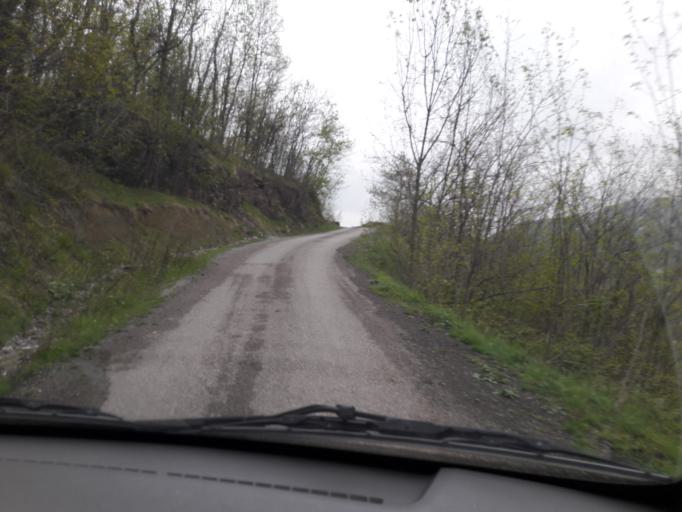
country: TR
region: Trabzon
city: Duzkoy
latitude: 40.9273
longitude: 39.4828
